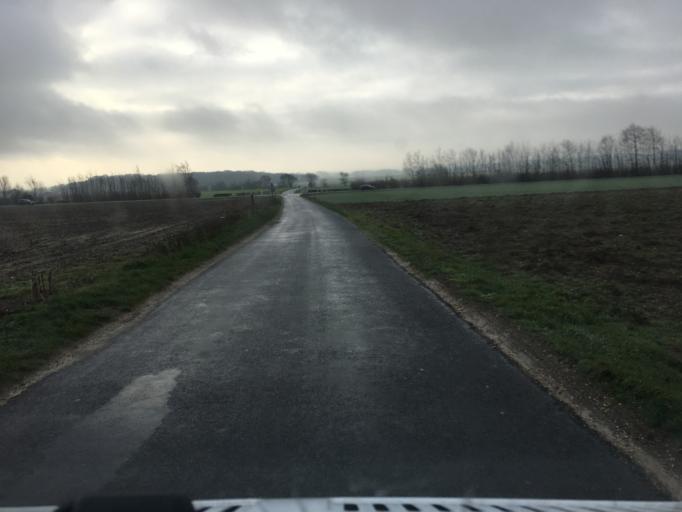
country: FR
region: Picardie
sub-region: Departement de la Somme
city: Saint-Valery-sur-Somme
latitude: 50.1759
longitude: 1.6200
